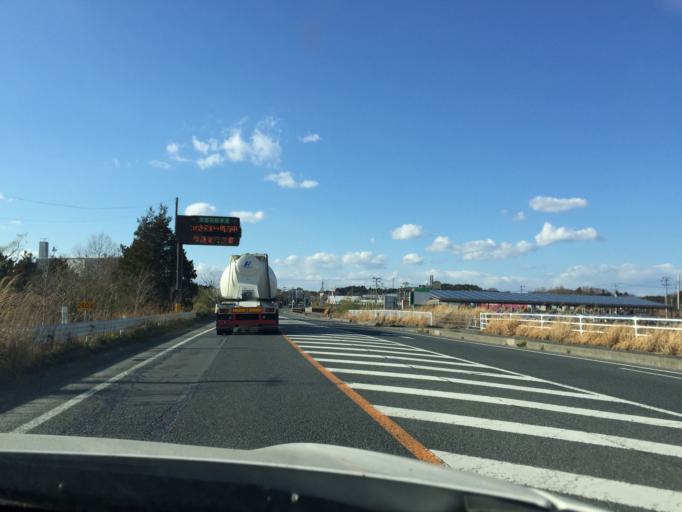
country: JP
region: Fukushima
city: Namie
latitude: 37.4922
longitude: 141.0032
